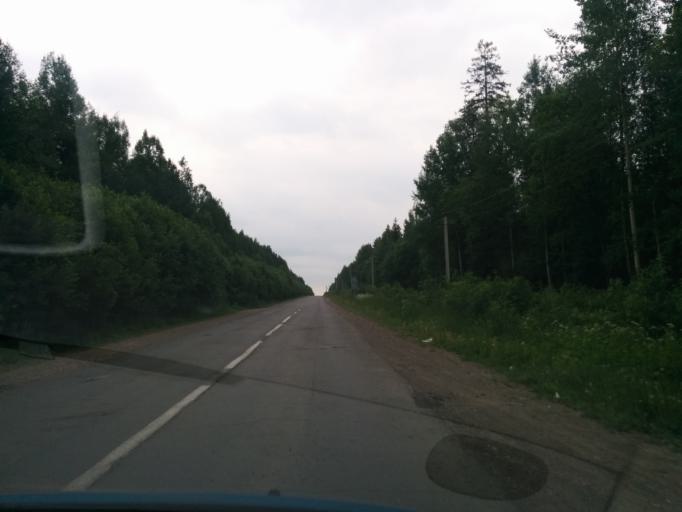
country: RU
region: Perm
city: Perm
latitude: 58.1970
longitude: 56.2114
